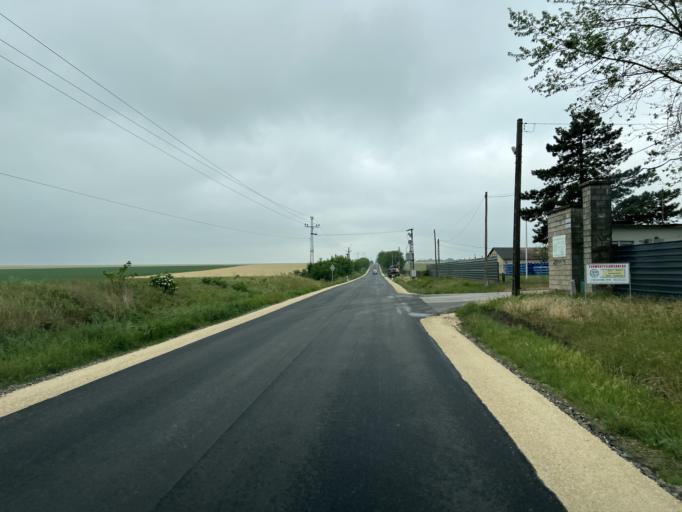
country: HU
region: Pest
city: Galgaheviz
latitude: 47.5938
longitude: 19.5768
